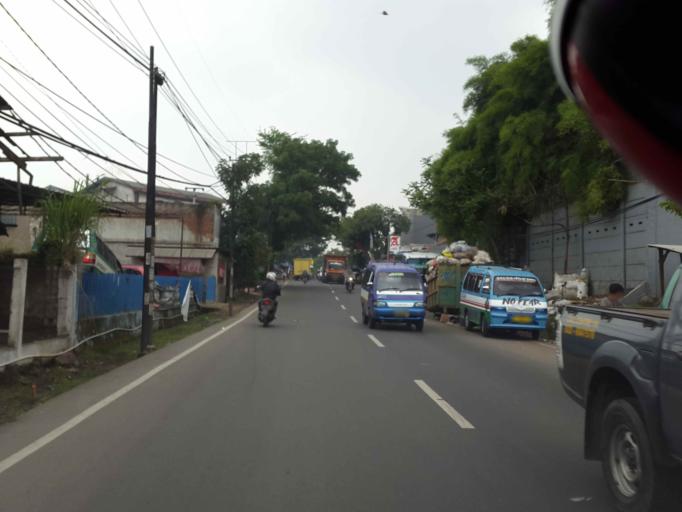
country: ID
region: West Java
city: Cimahi
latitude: -6.9020
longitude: 107.5421
